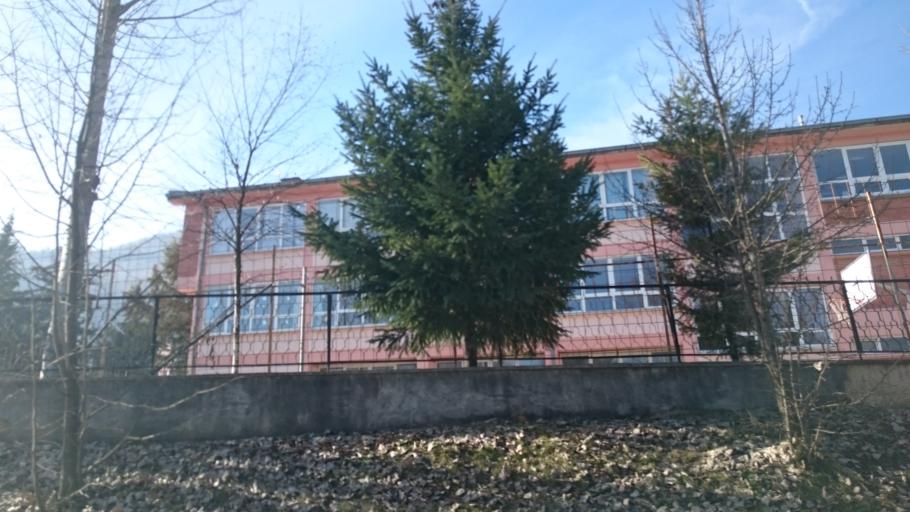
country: MK
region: Makedonski Brod
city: Makedonski Brod
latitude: 41.5116
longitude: 21.2165
